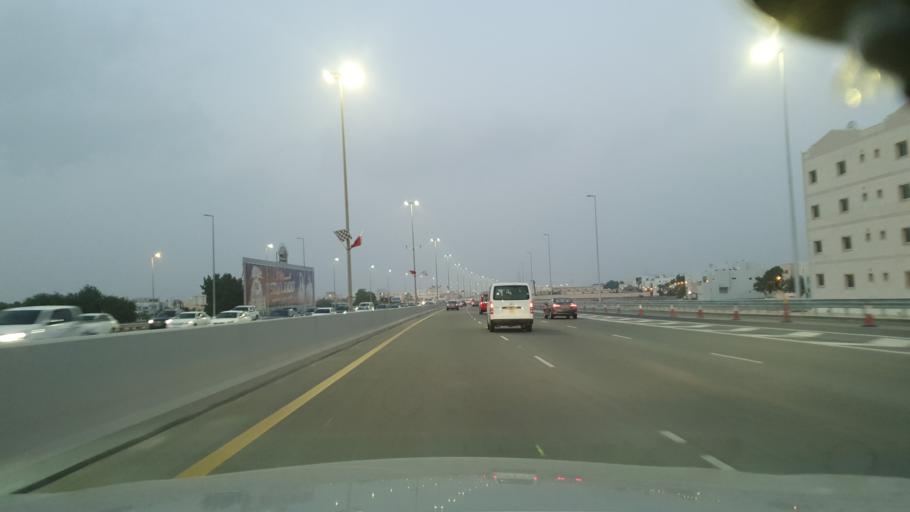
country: BH
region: Northern
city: Madinat `Isa
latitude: 26.1911
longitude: 50.5058
